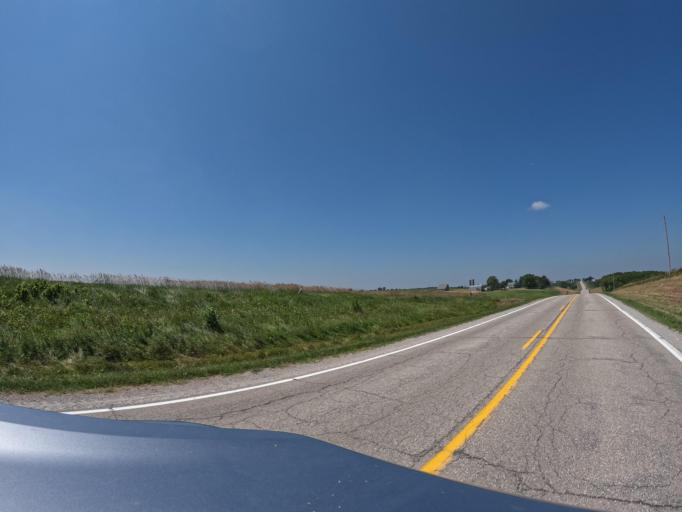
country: US
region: Iowa
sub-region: Keokuk County
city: Sigourney
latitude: 41.2649
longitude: -92.2113
